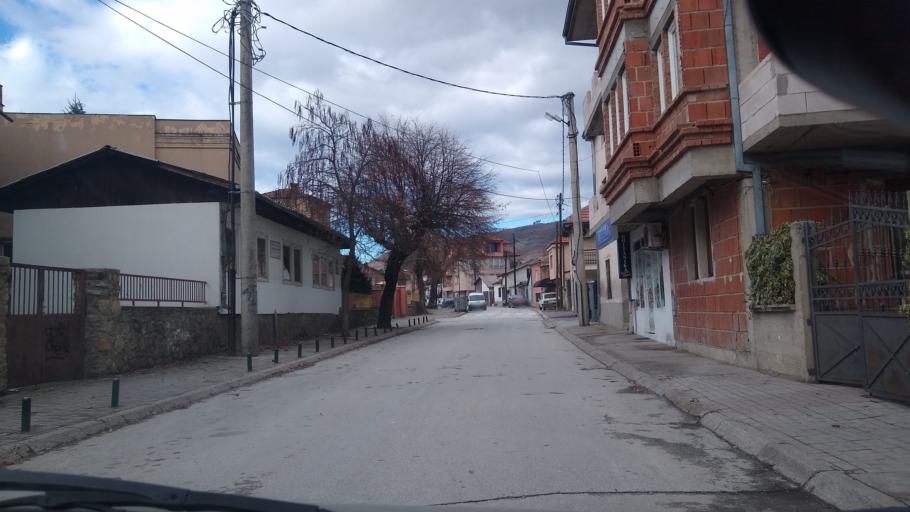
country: MK
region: Bitola
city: Bitola
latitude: 41.0275
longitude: 21.3271
